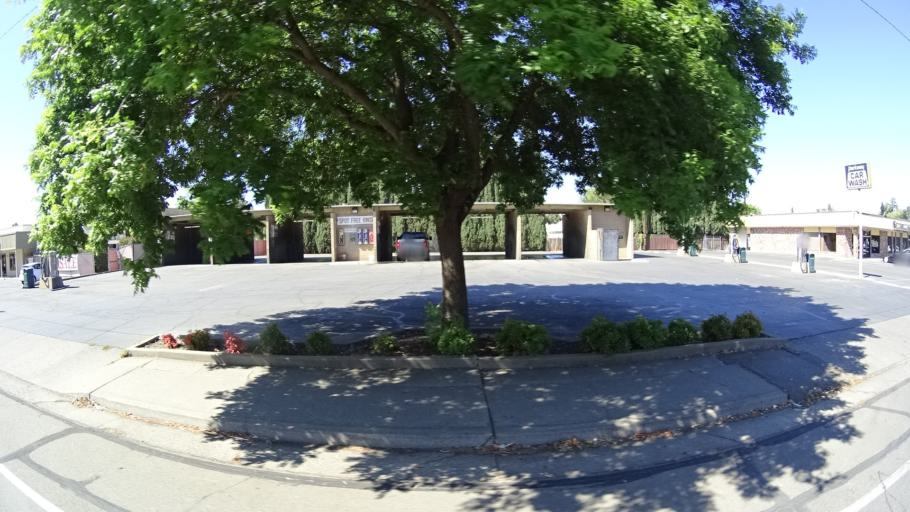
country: US
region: California
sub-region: Sacramento County
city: Elk Grove
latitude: 38.4057
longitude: -121.3715
